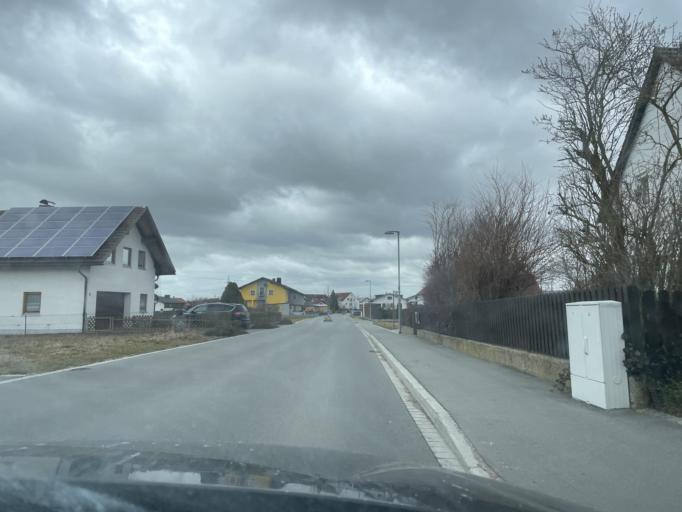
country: DE
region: Bavaria
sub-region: Upper Palatinate
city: Cham
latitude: 49.1975
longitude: 12.6817
